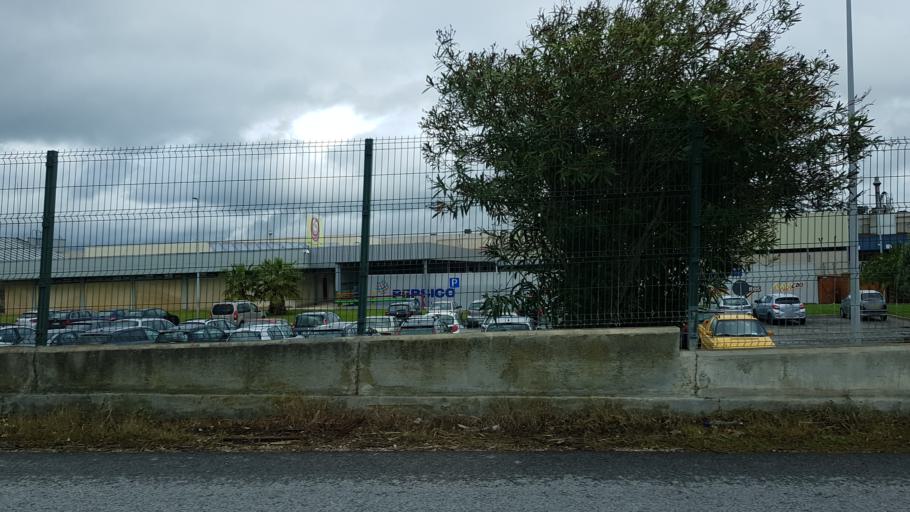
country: PT
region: Lisbon
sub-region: Alenquer
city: Carregado
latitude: 39.0341
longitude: -8.9761
